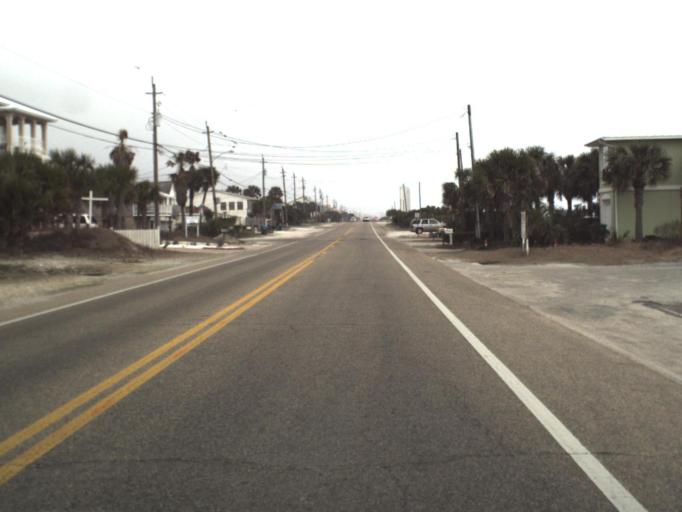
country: US
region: Florida
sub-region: Bay County
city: Laguna Beach
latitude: 30.2418
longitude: -85.9295
